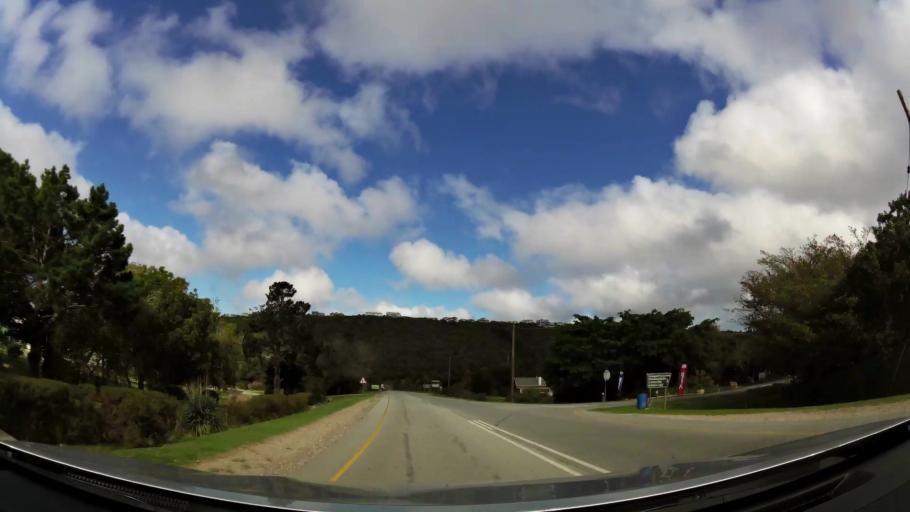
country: ZA
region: Western Cape
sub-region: Eden District Municipality
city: Plettenberg Bay
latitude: -34.0600
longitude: 23.3540
